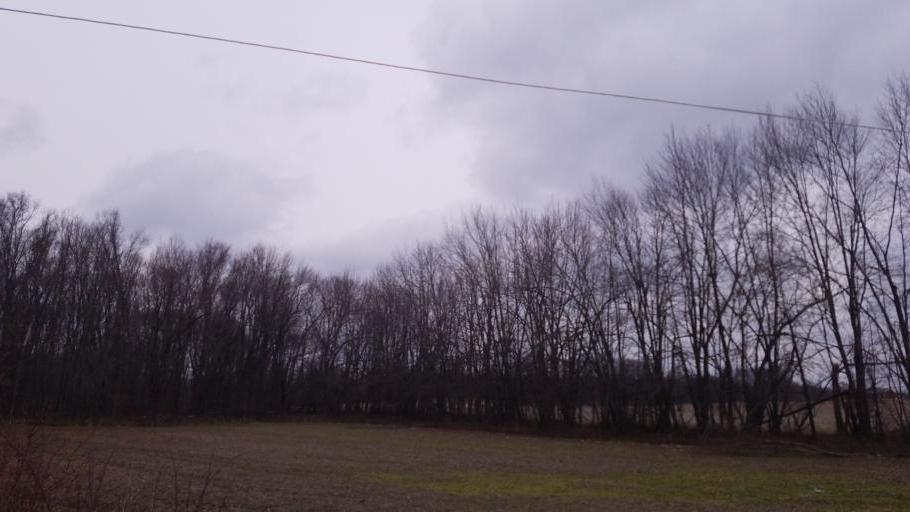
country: US
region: Ohio
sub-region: Crawford County
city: Crestline
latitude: 40.7493
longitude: -82.6867
